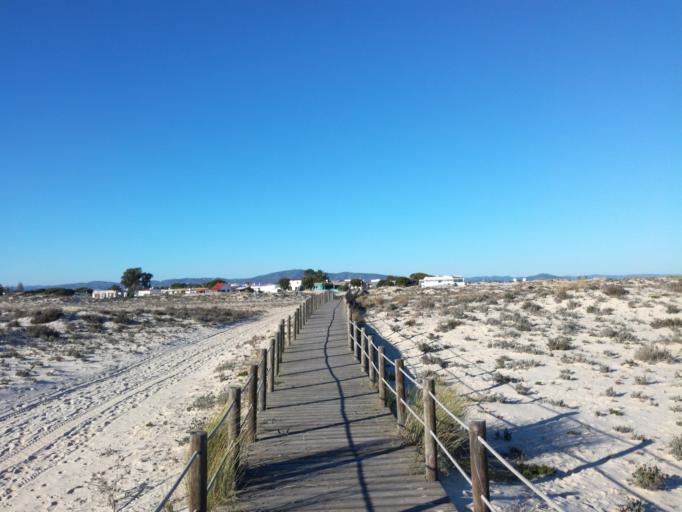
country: PT
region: Faro
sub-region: Olhao
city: Olhao
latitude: 37.0144
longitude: -7.7968
